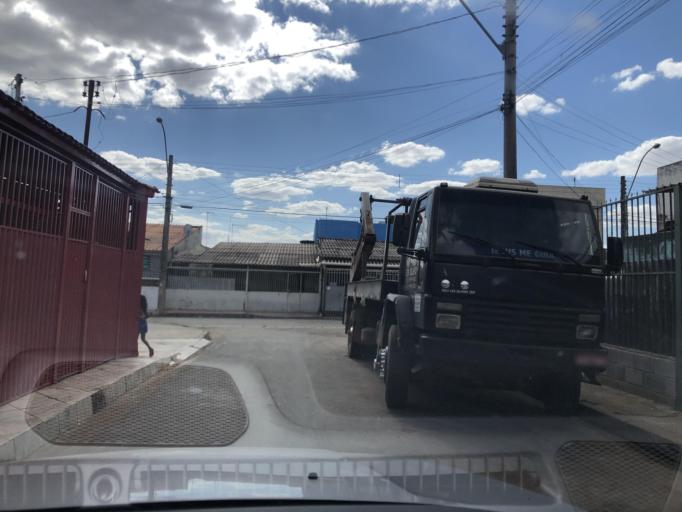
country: BR
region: Federal District
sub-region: Brasilia
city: Brasilia
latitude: -15.8943
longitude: -48.1426
